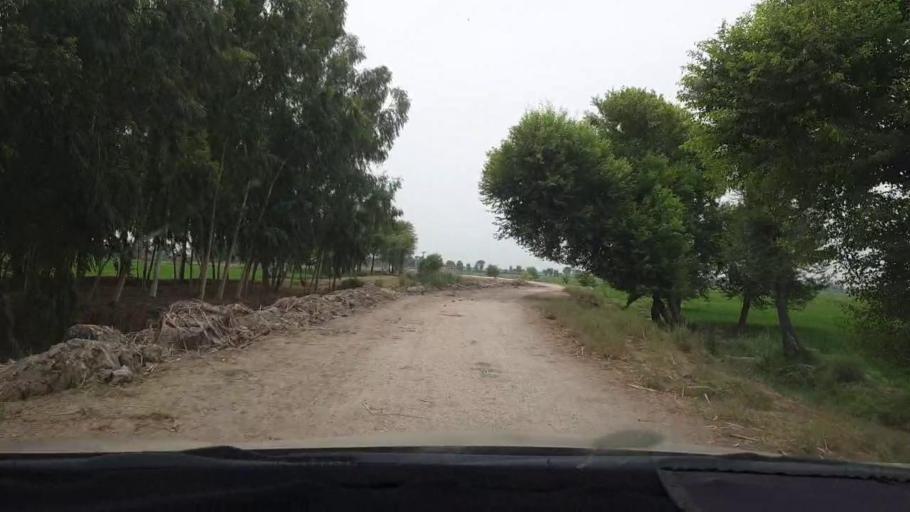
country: PK
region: Sindh
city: Ratodero
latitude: 27.7586
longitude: 68.3101
